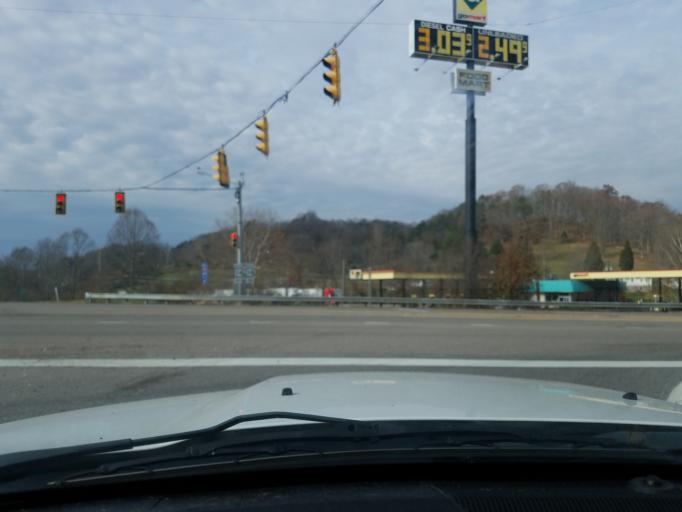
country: US
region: West Virginia
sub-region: Putnam County
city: Teays Valley
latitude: 38.4568
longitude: -81.9348
